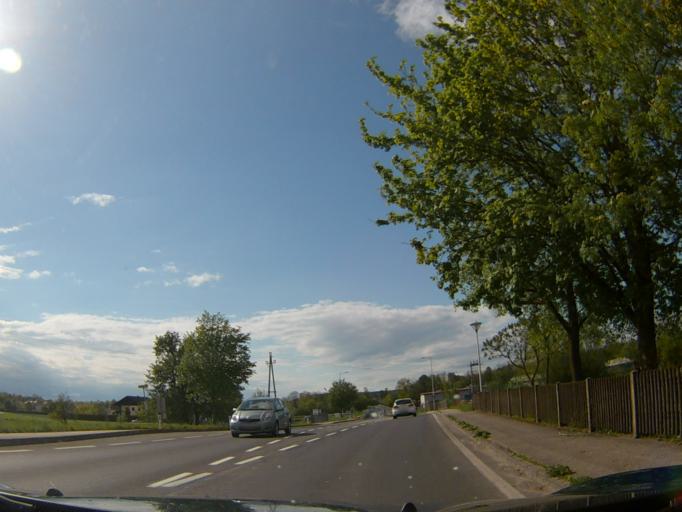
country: AT
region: Upper Austria
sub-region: Politischer Bezirk Vocklabruck
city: Rustorf
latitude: 48.0435
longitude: 13.7878
